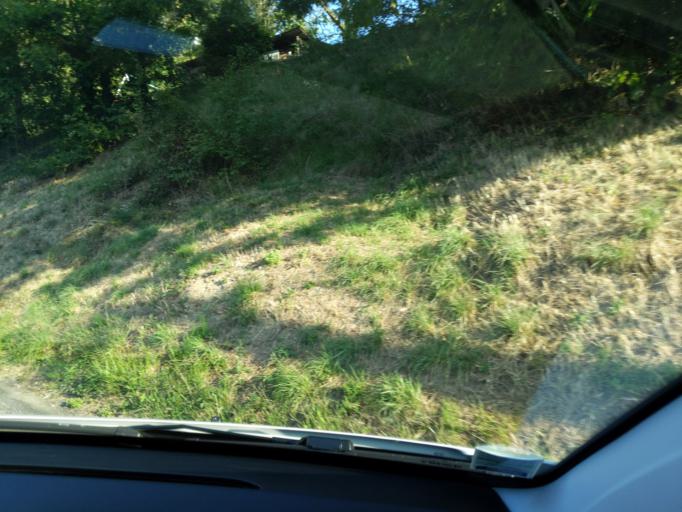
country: FR
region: Rhone-Alpes
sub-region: Departement de la Savoie
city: Aiton
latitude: 45.5628
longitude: 6.2752
